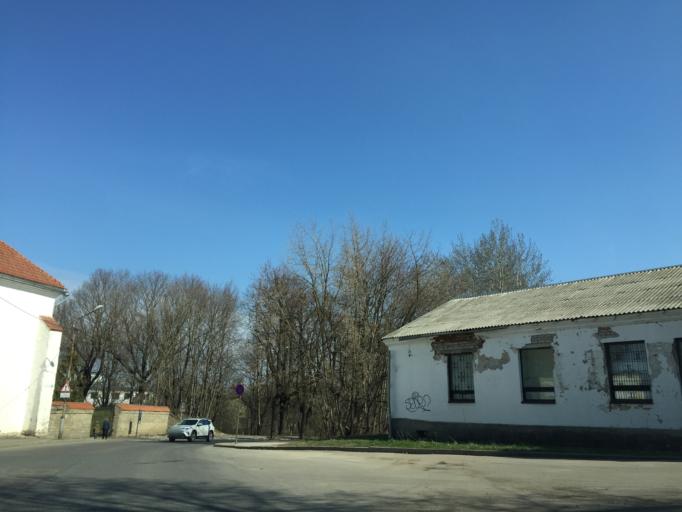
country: EE
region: Ida-Virumaa
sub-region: Narva linn
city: Narva
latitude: 59.3820
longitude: 28.1968
